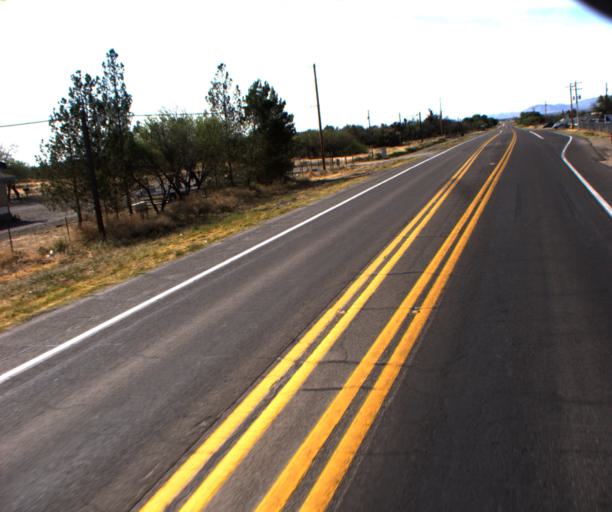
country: US
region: Arizona
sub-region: Graham County
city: Cactus Flat
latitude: 32.7676
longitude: -109.7164
